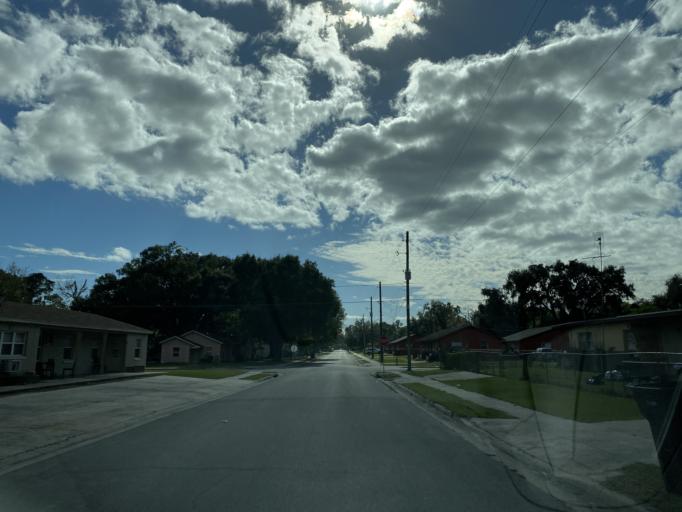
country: US
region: Florida
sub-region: Orange County
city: Orlando
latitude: 28.5233
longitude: -81.3909
